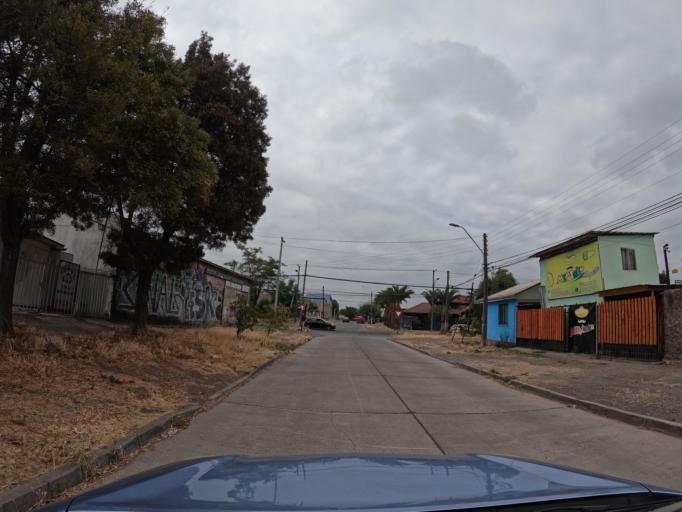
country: CL
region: Maule
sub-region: Provincia de Curico
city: Curico
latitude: -34.9756
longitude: -71.2513
